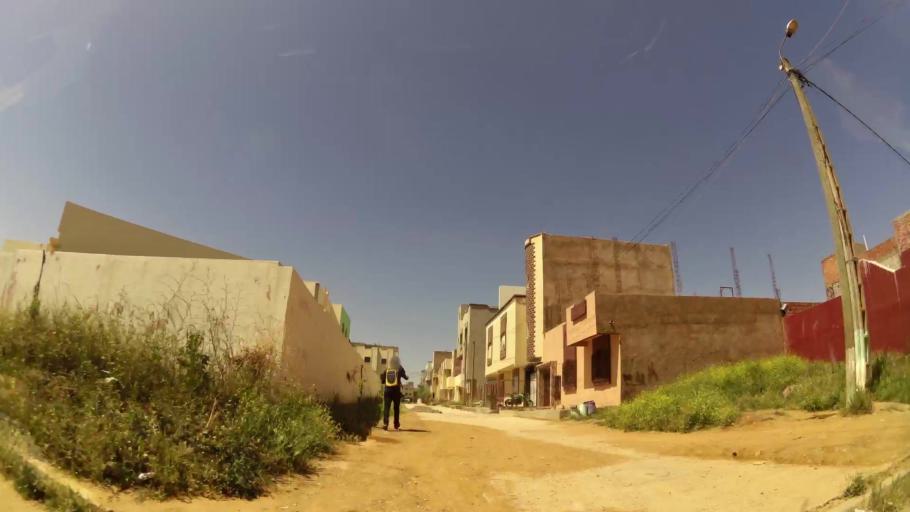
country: MA
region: Rabat-Sale-Zemmour-Zaer
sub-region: Khemisset
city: Khemisset
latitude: 33.8086
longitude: -6.0844
